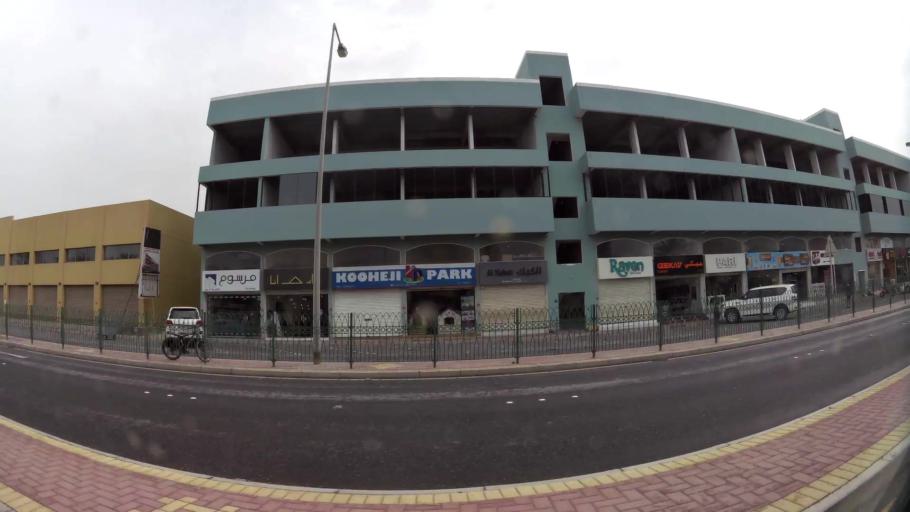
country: BH
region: Northern
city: Ar Rifa'
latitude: 26.1348
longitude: 50.5509
